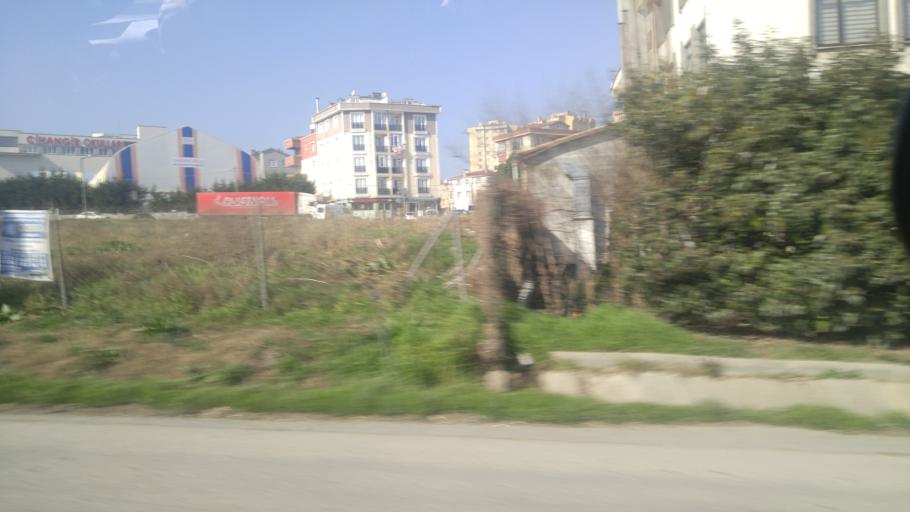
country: TR
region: Istanbul
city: Chekmejeh
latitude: 41.0130
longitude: 28.5397
